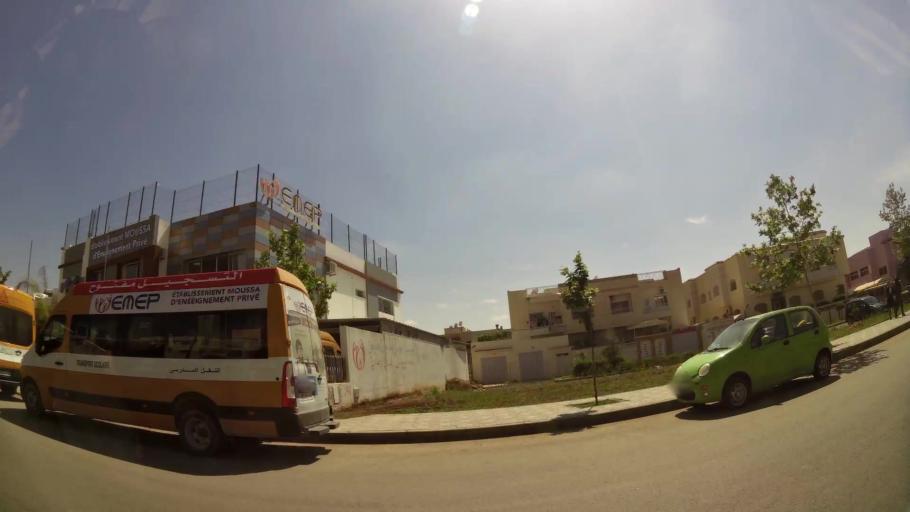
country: MA
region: Fes-Boulemane
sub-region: Fes
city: Fes
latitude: 34.0194
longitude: -5.0231
